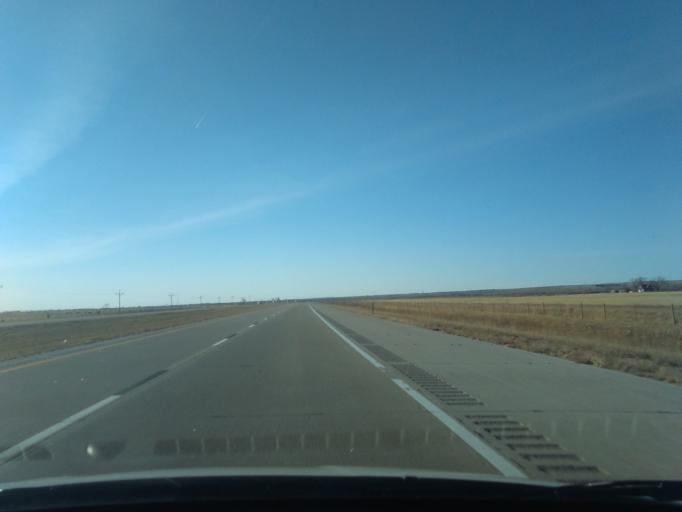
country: US
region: Colorado
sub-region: Sedgwick County
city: Julesburg
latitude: 41.0626
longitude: -101.9986
